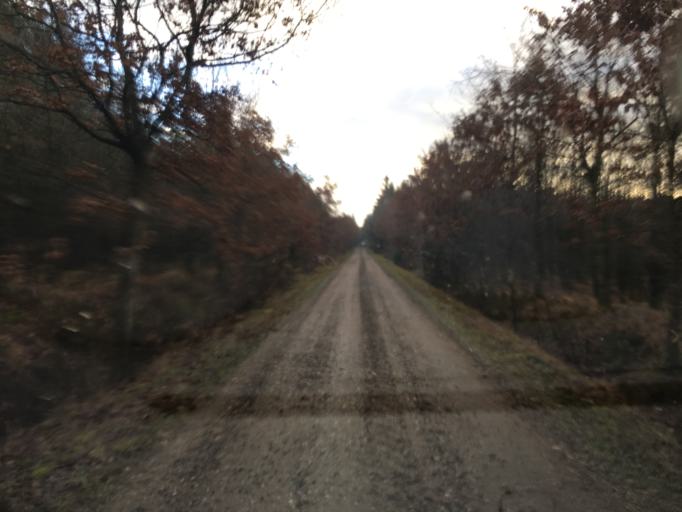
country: DK
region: South Denmark
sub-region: Tonder Kommune
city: Sherrebek
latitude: 55.1300
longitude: 8.8724
